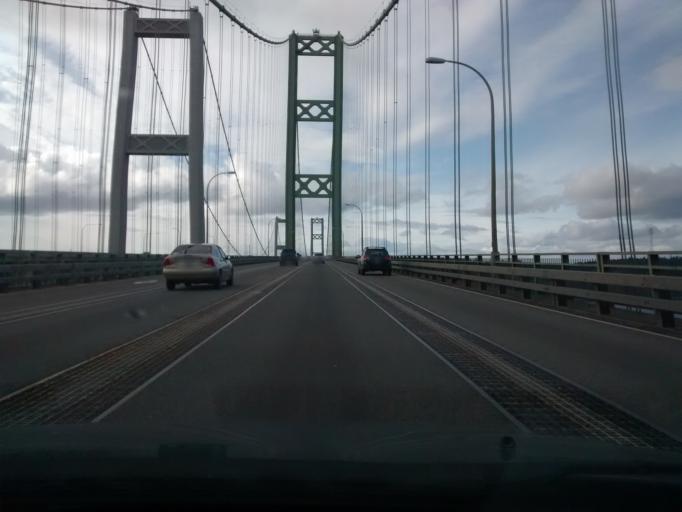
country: US
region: Washington
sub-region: Pierce County
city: University Place
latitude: 47.2637
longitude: -122.5445
